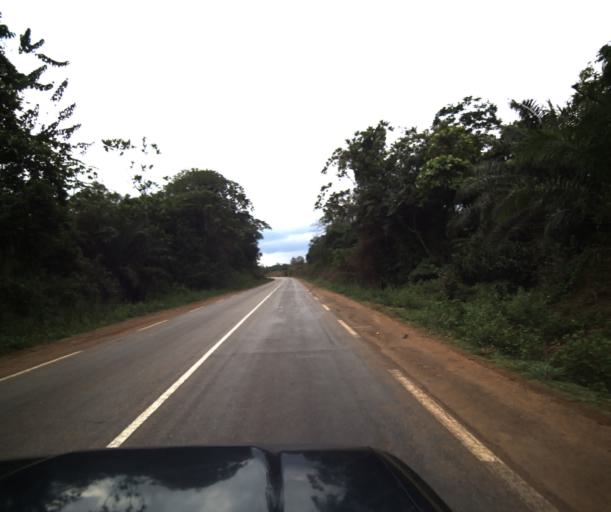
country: CM
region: Littoral
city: Edea
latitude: 3.9457
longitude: 10.0427
